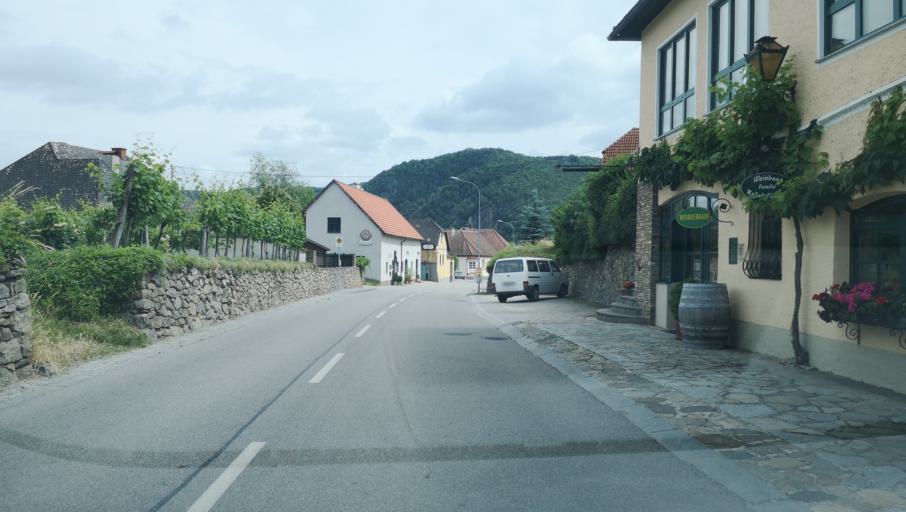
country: AT
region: Lower Austria
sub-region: Politischer Bezirk Krems
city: Durnstein
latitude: 48.3896
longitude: 15.5145
